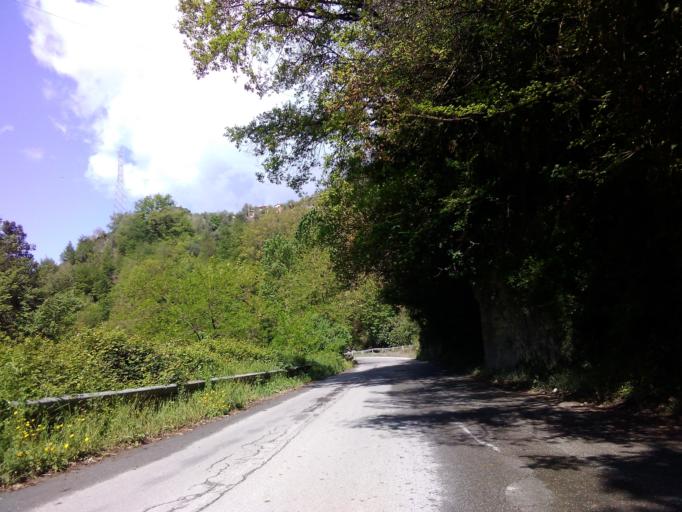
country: IT
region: Tuscany
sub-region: Provincia di Massa-Carrara
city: Carrara
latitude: 44.0824
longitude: 10.1111
